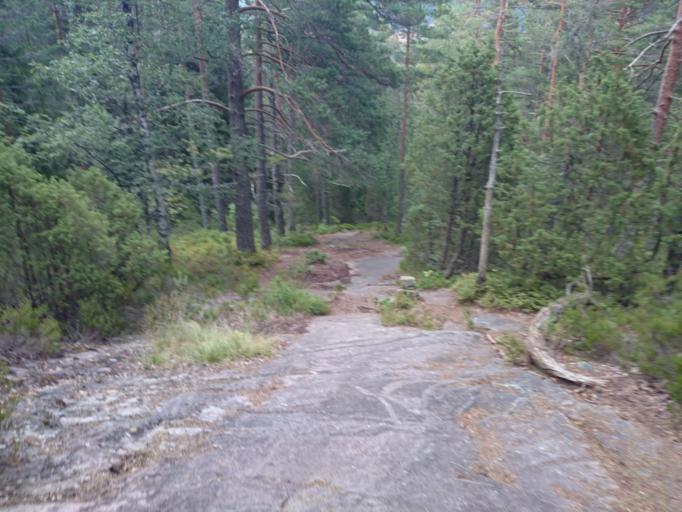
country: NO
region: Aust-Agder
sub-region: Amli
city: Amli
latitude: 58.7692
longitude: 8.4694
